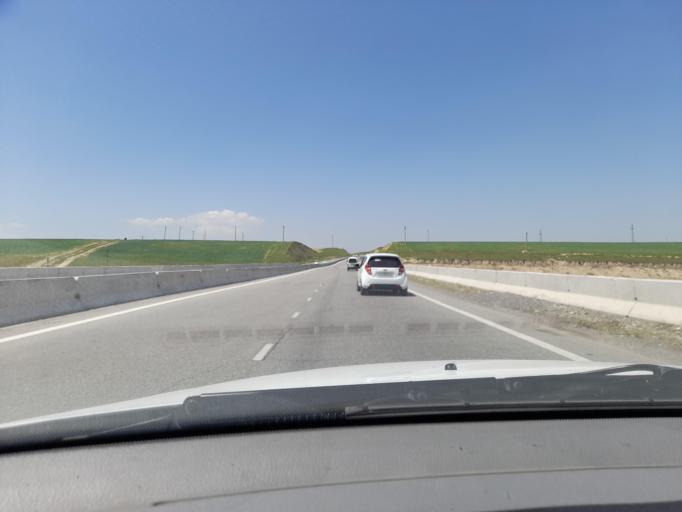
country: UZ
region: Jizzax
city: Jizzax
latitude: 40.0470
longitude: 67.7395
